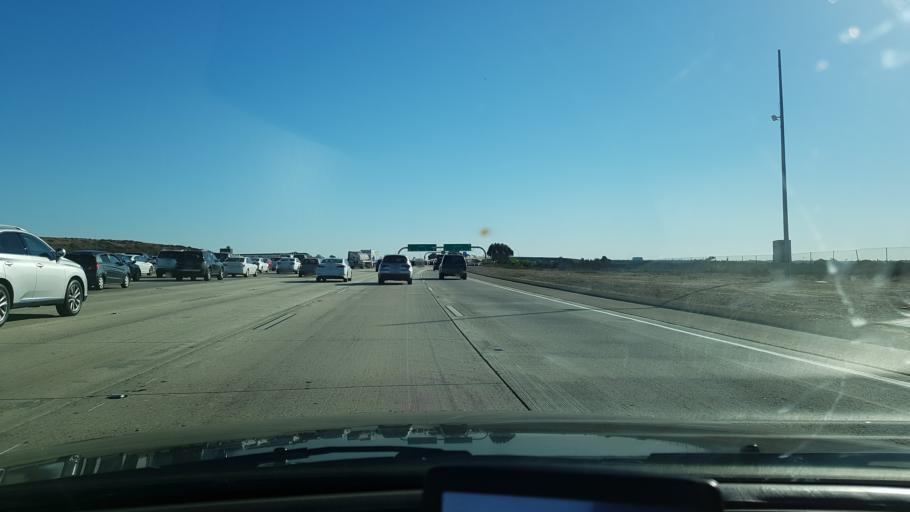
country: US
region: California
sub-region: San Diego County
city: Poway
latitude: 32.8689
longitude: -117.1083
